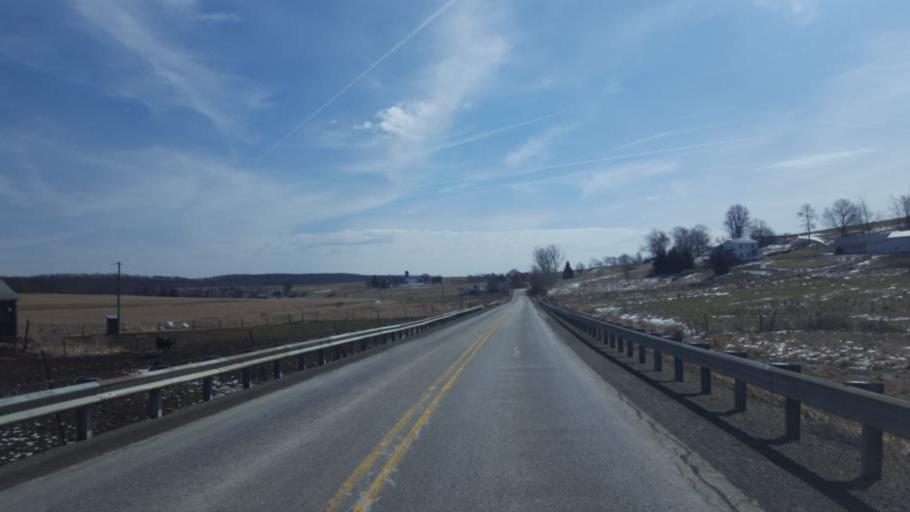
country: US
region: Pennsylvania
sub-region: Potter County
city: Galeton
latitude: 41.8938
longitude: -77.7468
